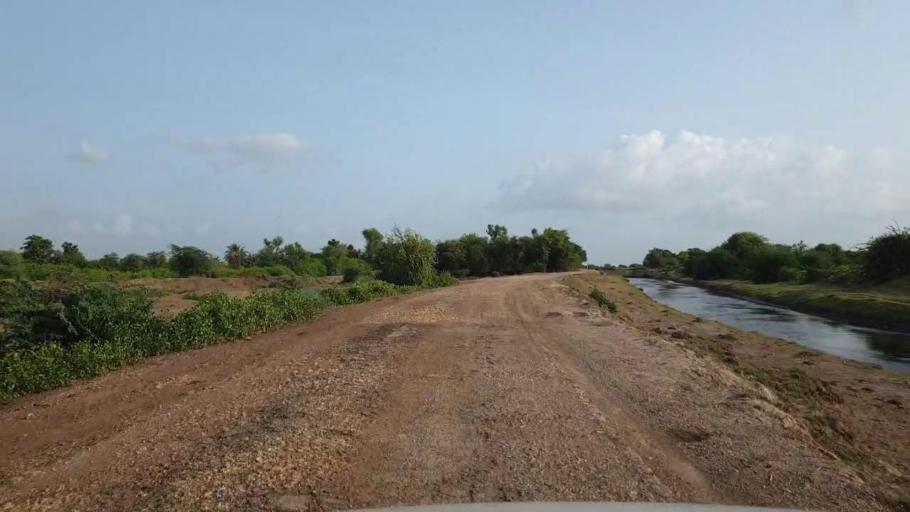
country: PK
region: Sindh
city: Kario
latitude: 24.8373
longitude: 68.6522
